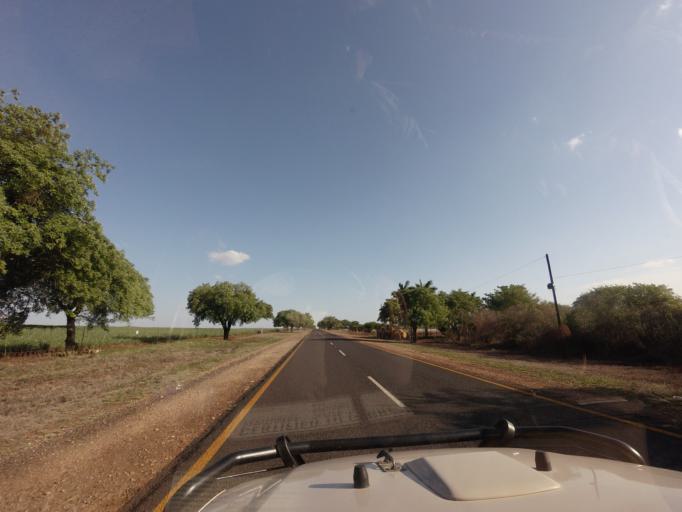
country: ZA
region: Mpumalanga
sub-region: Ehlanzeni District
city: Komatipoort
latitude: -25.3719
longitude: 31.9044
